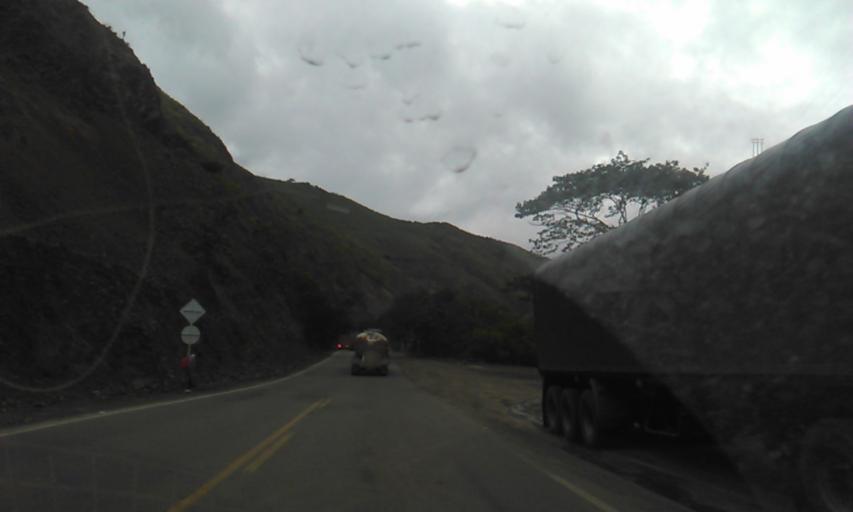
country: CO
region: Valle del Cauca
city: Dagua
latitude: 3.7803
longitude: -76.6466
